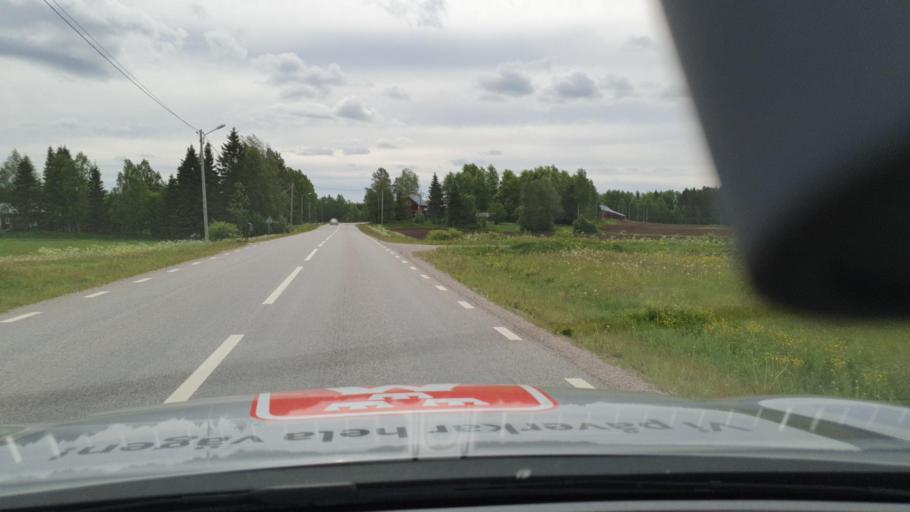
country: SE
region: Norrbotten
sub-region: Kalix Kommun
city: Kalix
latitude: 65.9442
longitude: 23.4564
